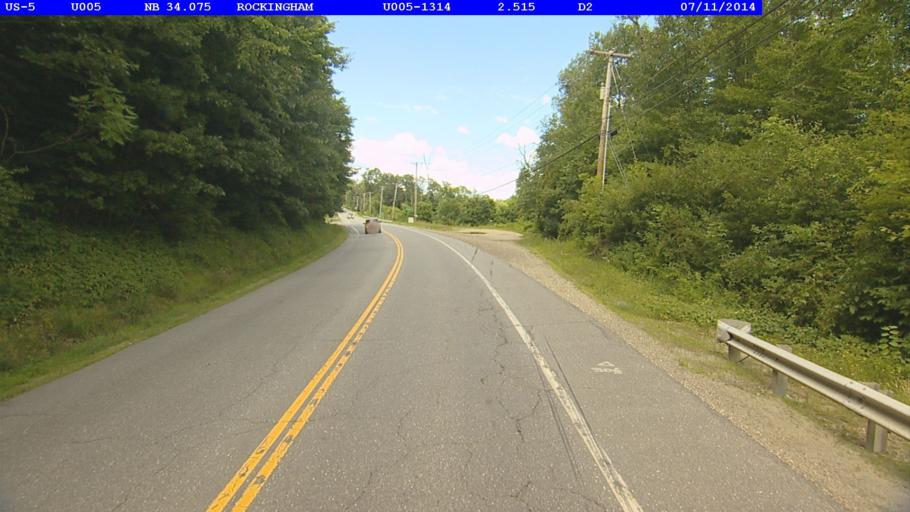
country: US
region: Vermont
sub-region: Windham County
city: Bellows Falls
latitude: 43.1574
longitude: -72.4578
